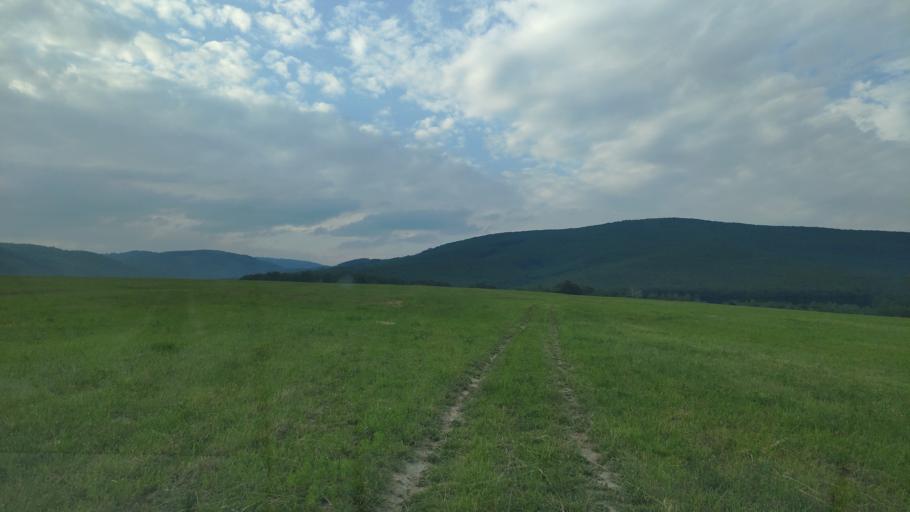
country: SK
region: Kosicky
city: Moldava nad Bodvou
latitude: 48.7108
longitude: 20.9930
